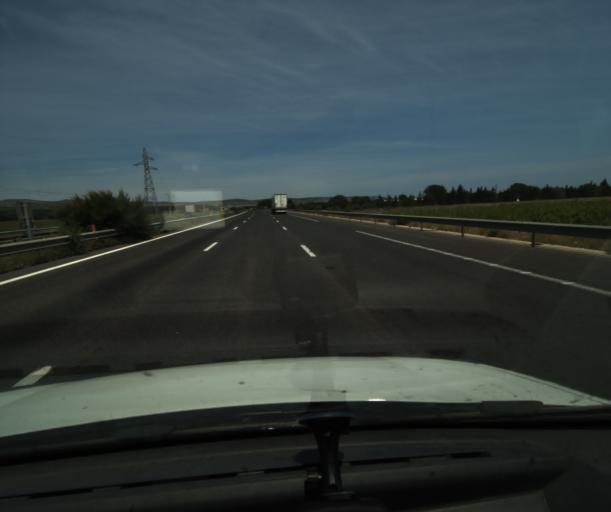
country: FR
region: Languedoc-Roussillon
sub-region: Departement des Pyrenees-Orientales
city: Salses-le-Chateau
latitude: 42.8099
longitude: 2.9041
